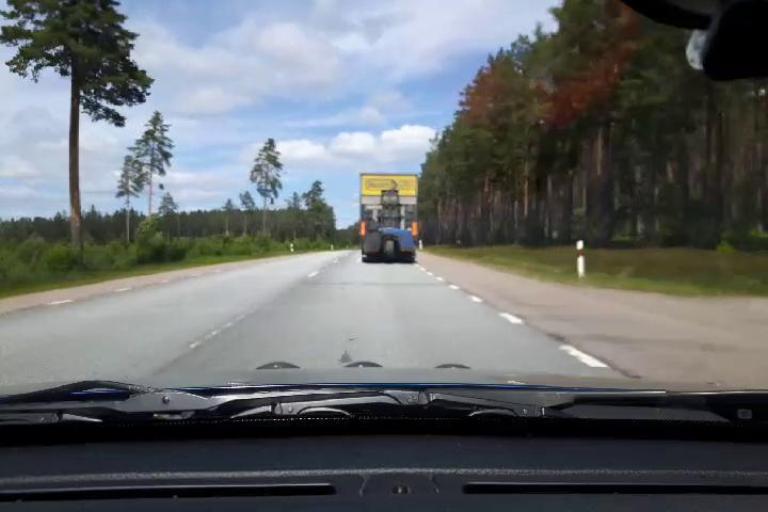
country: SE
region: Uppsala
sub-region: Tierps Kommun
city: Tierp
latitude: 60.1955
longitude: 17.4800
